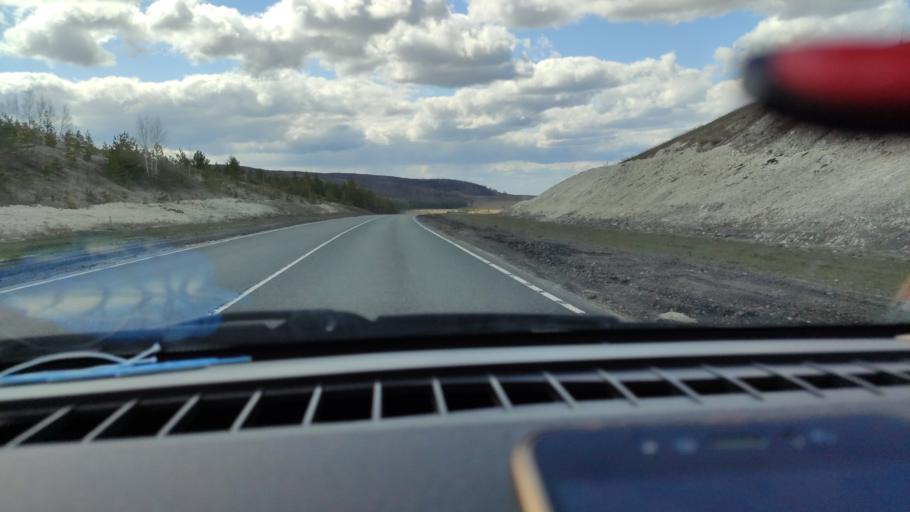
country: RU
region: Saratov
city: Alekseyevka
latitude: 52.3668
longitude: 47.9629
